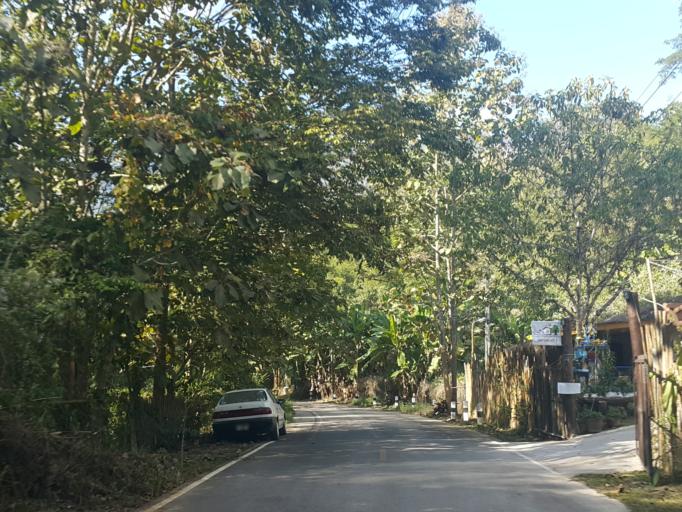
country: TH
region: Chiang Mai
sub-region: Amphoe Chiang Dao
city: Chiang Dao
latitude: 19.4093
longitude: 98.9232
